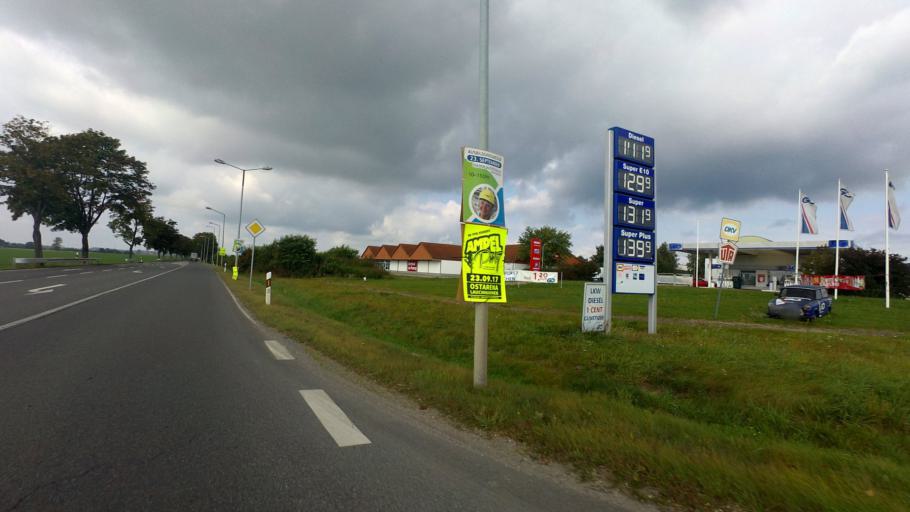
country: DE
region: Brandenburg
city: Plessa
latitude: 51.4656
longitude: 13.6058
